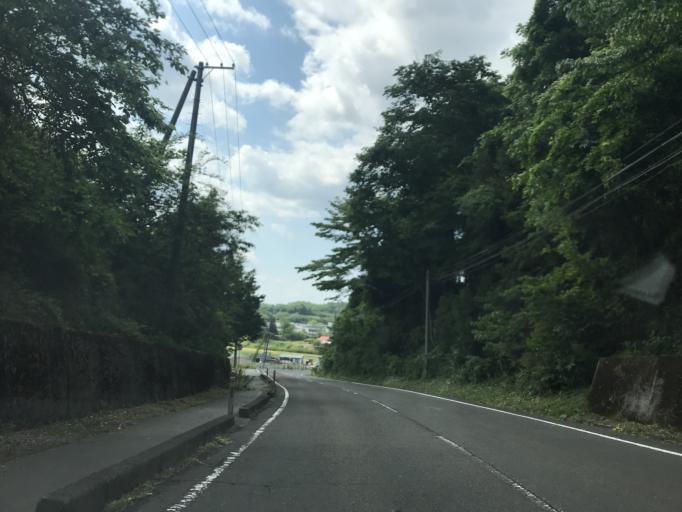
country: JP
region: Miyagi
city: Furukawa
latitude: 38.7713
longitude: 140.9627
